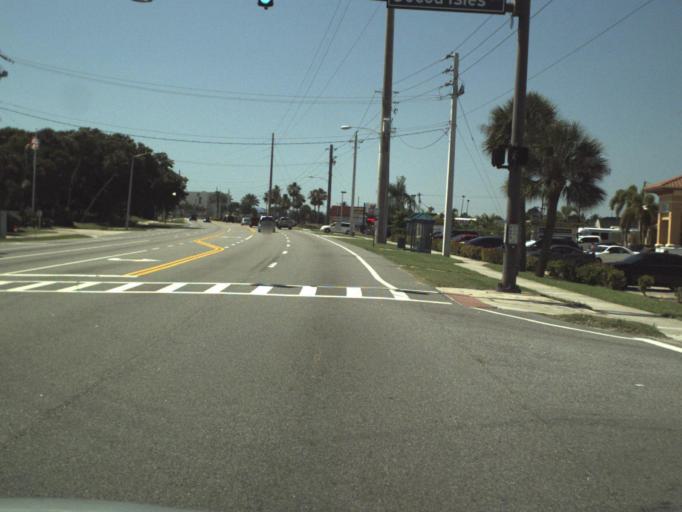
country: US
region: Florida
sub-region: Brevard County
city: Cocoa Beach
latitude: 28.3297
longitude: -80.6106
